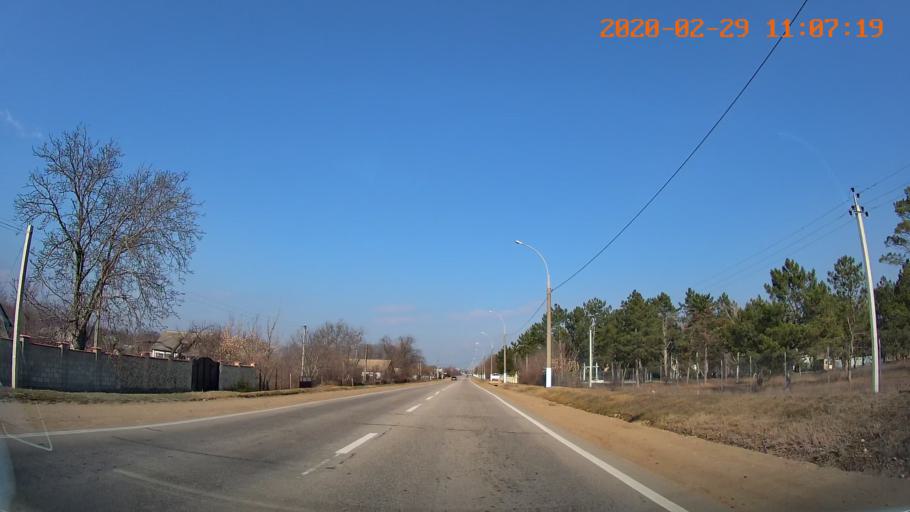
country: MD
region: Criuleni
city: Criuleni
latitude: 47.2242
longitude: 29.1829
